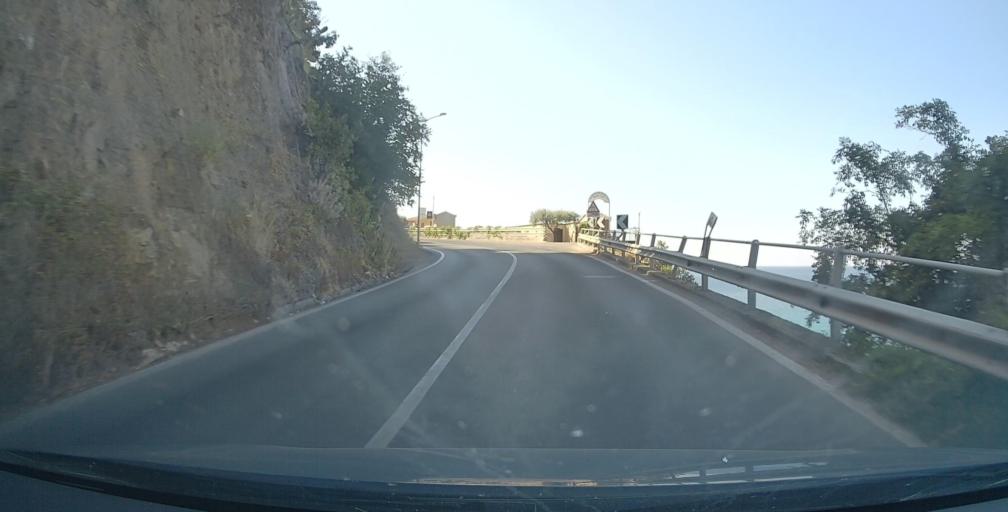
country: IT
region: Sicily
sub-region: Messina
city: Naso
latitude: 38.1521
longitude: 14.7826
